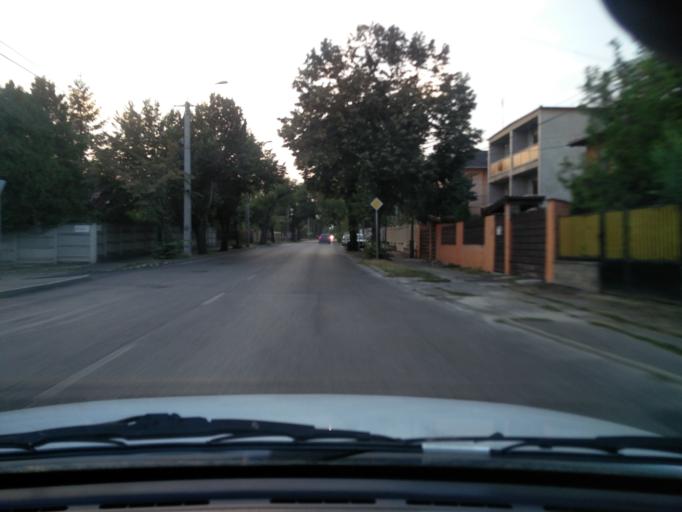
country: HU
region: Budapest
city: Budapest XXI. keruelet
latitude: 47.4115
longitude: 19.0880
